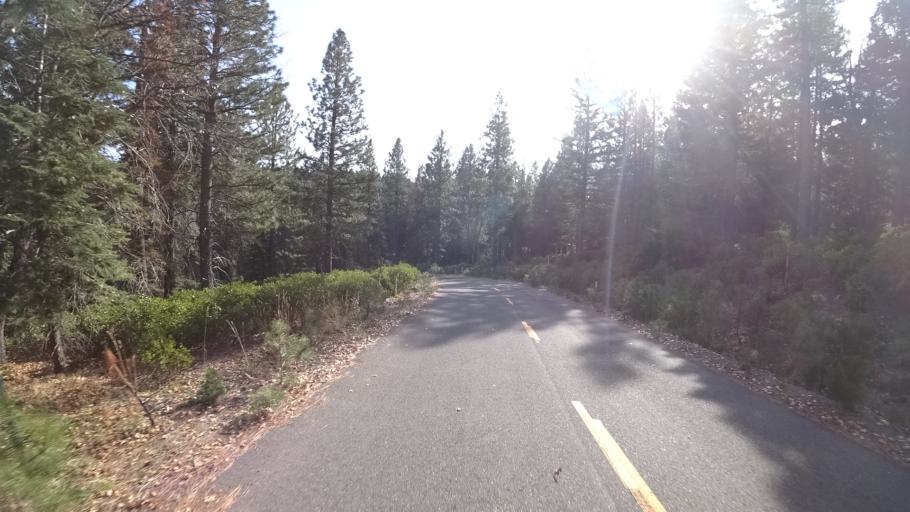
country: US
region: California
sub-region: Siskiyou County
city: Weed
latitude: 41.3932
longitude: -122.3921
